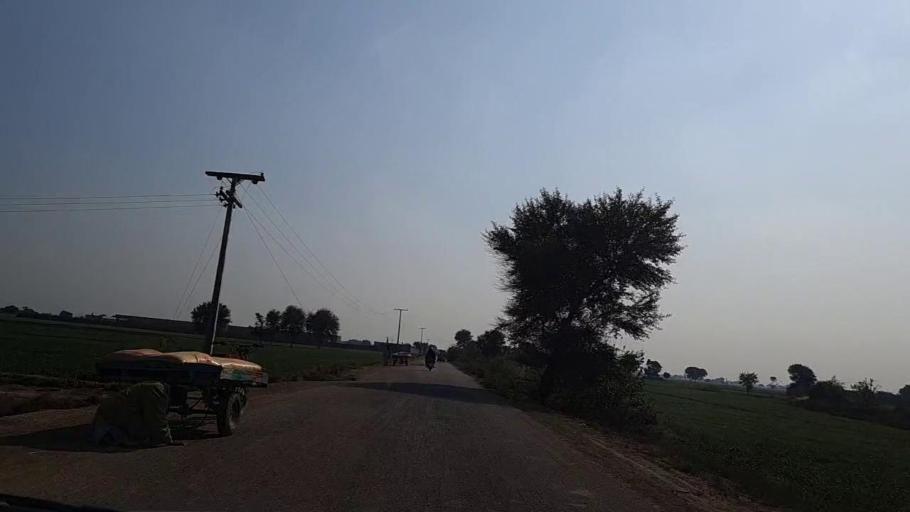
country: PK
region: Sindh
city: Sakrand
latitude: 26.1075
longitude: 68.2908
